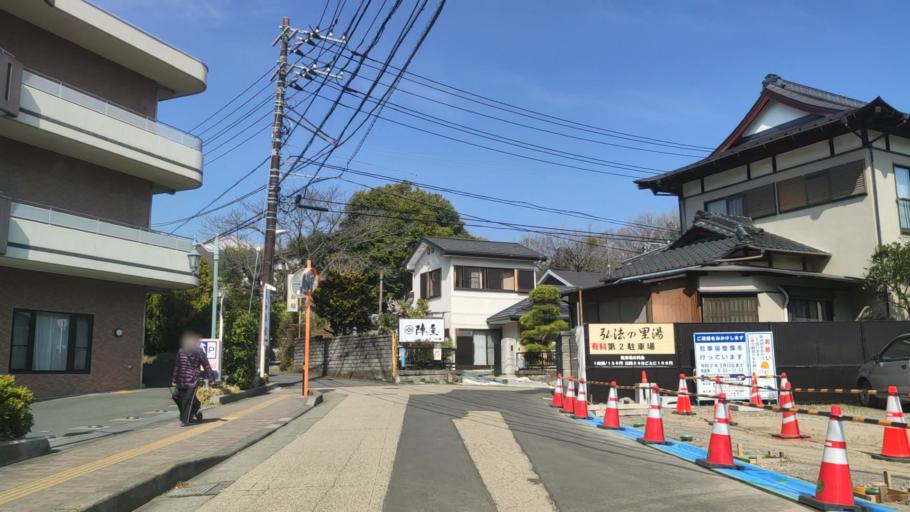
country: JP
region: Kanagawa
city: Isehara
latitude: 35.3820
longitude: 139.2768
